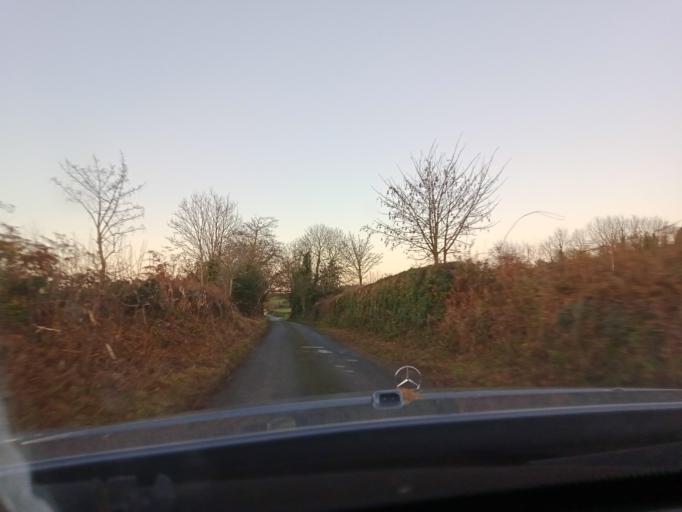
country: IE
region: Leinster
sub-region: Kilkenny
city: Thomastown
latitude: 52.4458
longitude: -7.1048
